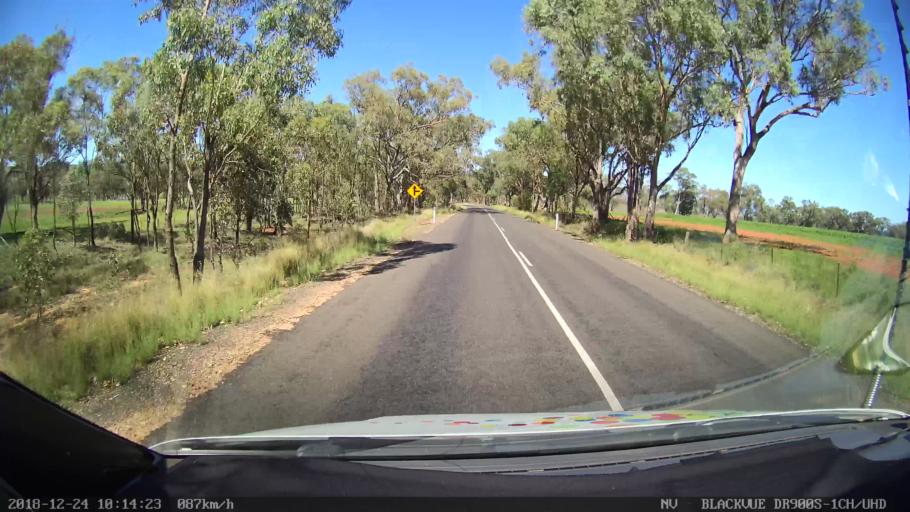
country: AU
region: New South Wales
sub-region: Liverpool Plains
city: Quirindi
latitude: -31.6972
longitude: 150.6287
